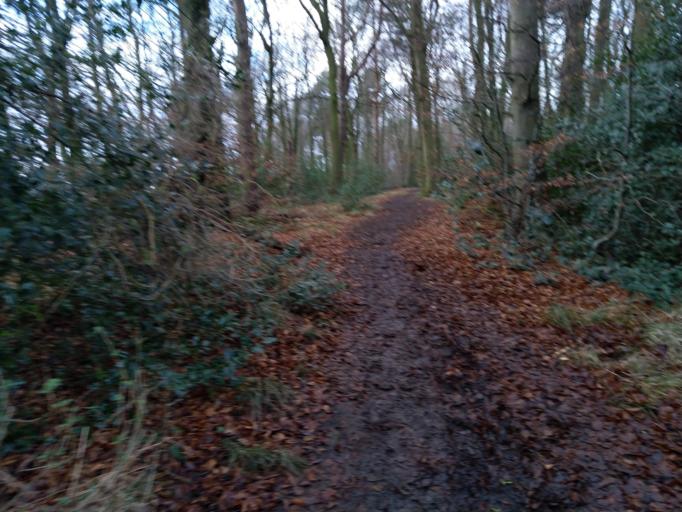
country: GB
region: Scotland
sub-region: Fife
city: Limekilns
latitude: 55.9989
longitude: -3.5147
